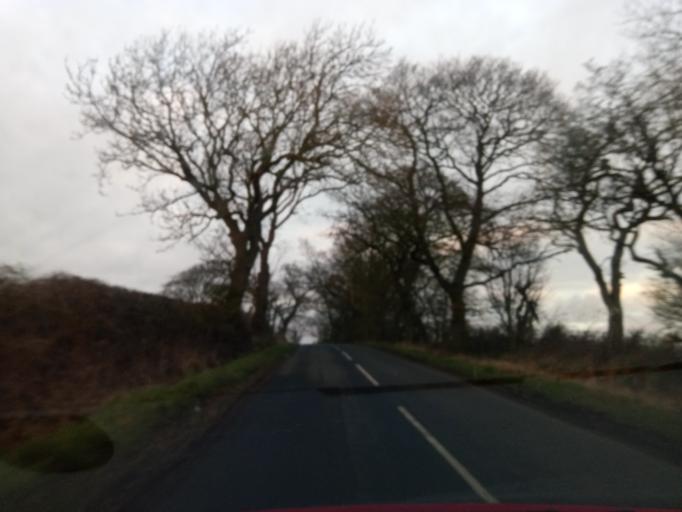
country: GB
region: England
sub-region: Northumberland
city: Meldon
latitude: 55.1345
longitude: -1.8014
